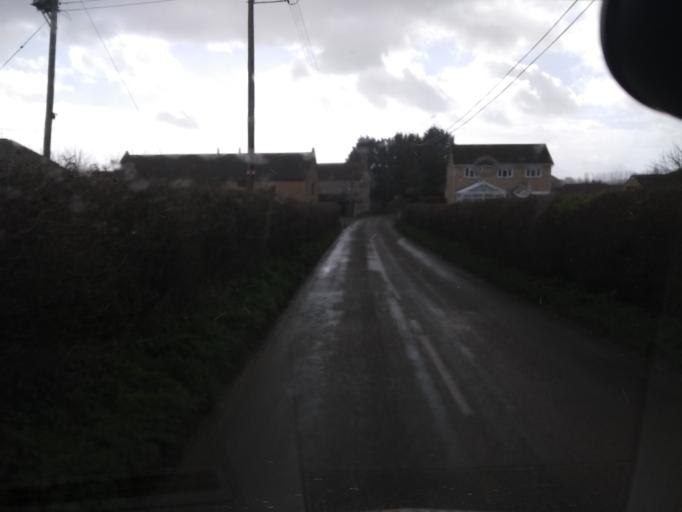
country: GB
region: England
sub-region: Somerset
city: South Petherton
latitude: 50.9790
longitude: -2.8194
